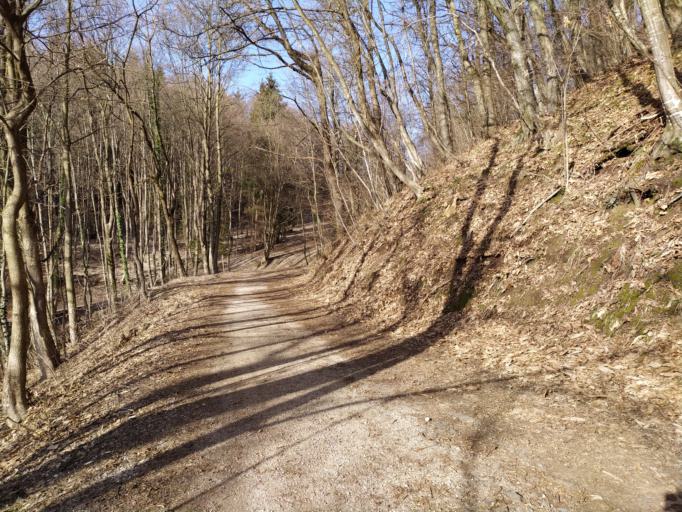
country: IT
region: Veneto
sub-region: Provincia di Vicenza
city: San Quirico
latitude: 45.6968
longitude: 11.2858
